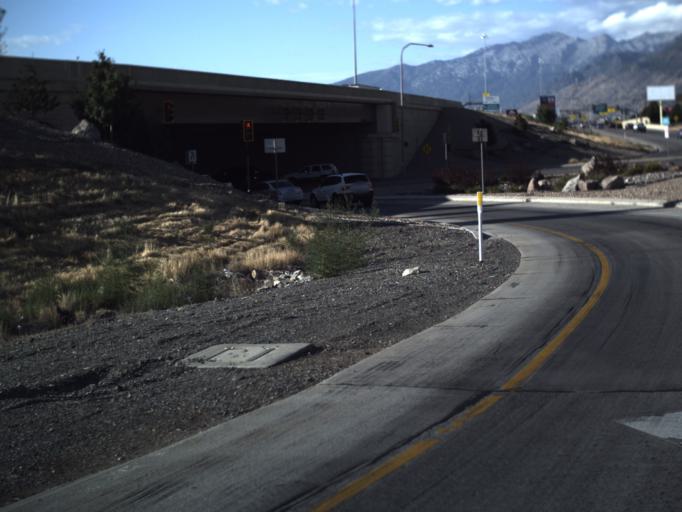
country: US
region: Utah
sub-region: Utah County
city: Orem
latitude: 40.2963
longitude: -111.7250
